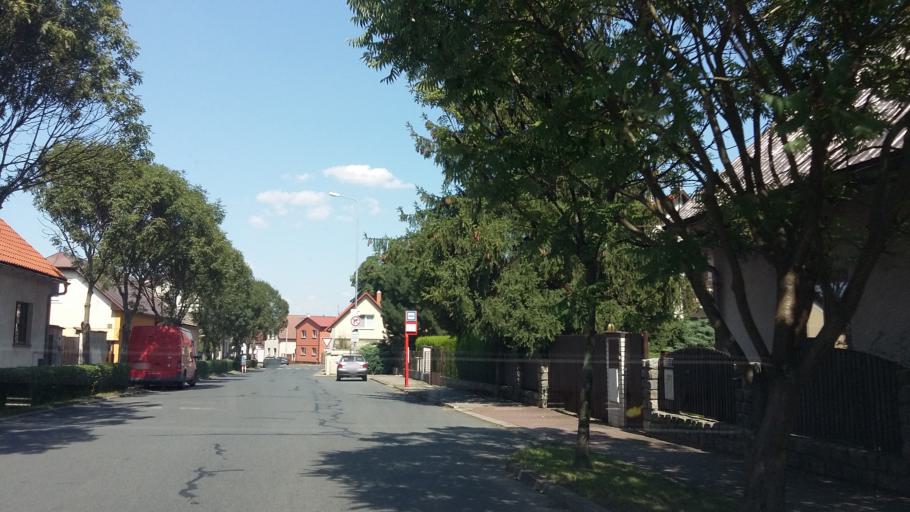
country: CZ
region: Central Bohemia
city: Zelenec
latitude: 50.1319
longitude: 14.6601
